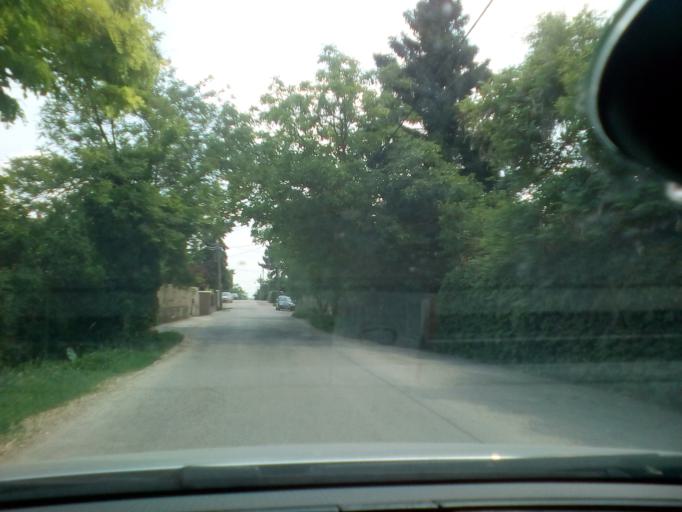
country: HU
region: Pest
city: Diosd
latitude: 47.3995
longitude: 18.9329
